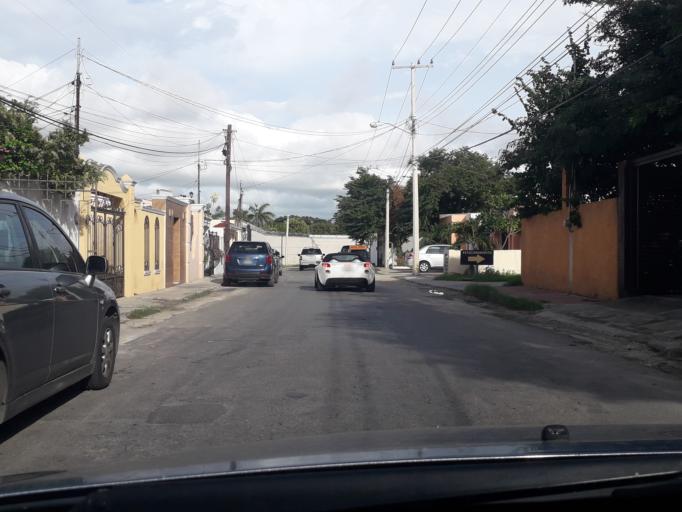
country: MX
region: Yucatan
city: Merida
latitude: 21.0039
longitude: -89.6400
